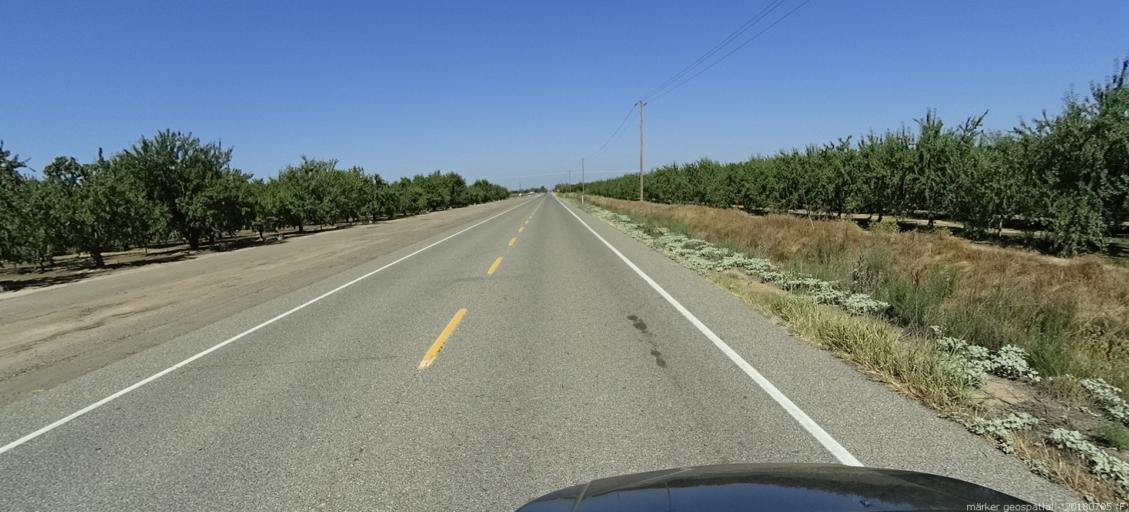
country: US
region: California
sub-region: Madera County
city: Fairmead
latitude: 37.0982
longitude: -120.1810
